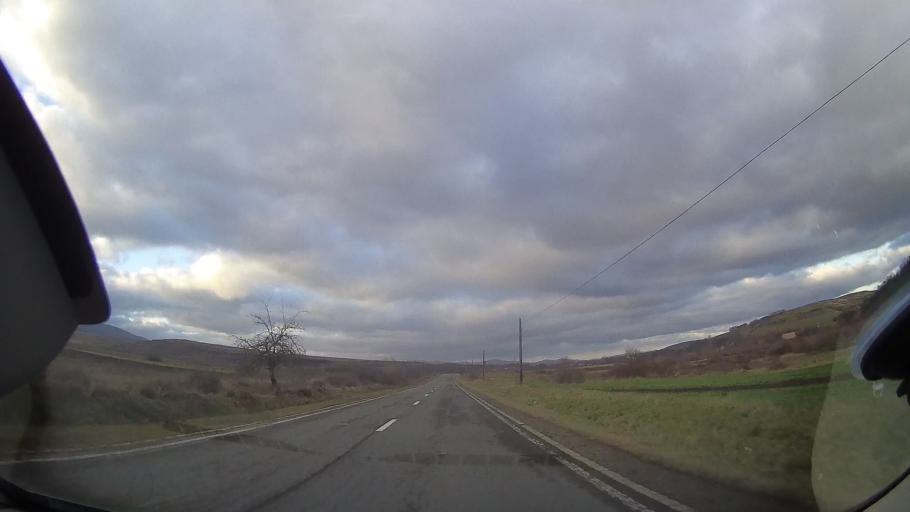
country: RO
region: Cluj
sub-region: Comuna Calatele
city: Calatele
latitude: 46.7888
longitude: 22.9990
